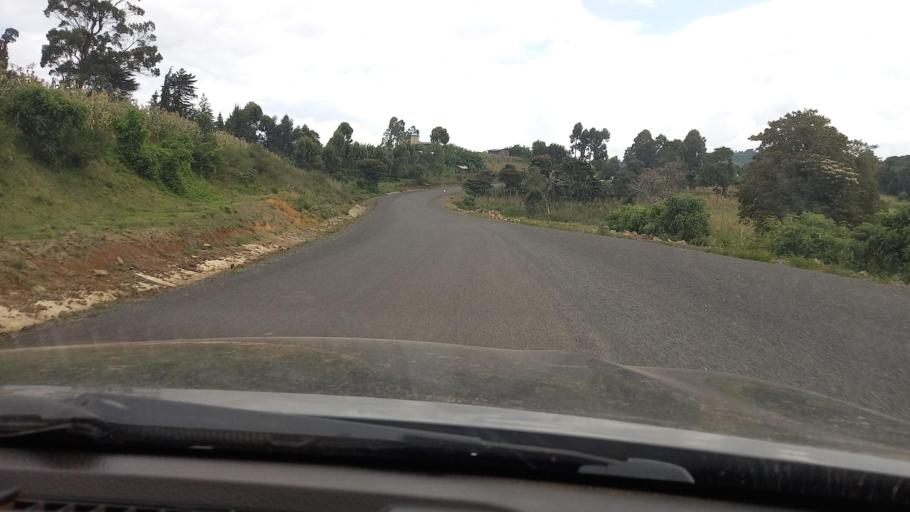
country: ET
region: Southern Nations, Nationalities, and People's Region
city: Mizan Teferi
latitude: 6.2127
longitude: 35.6141
